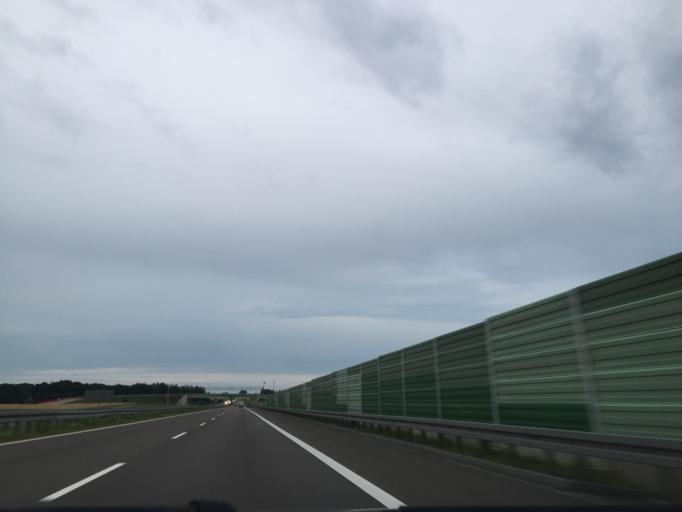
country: PL
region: Podlasie
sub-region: Powiat bialostocki
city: Choroszcz
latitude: 53.1597
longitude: 22.8955
